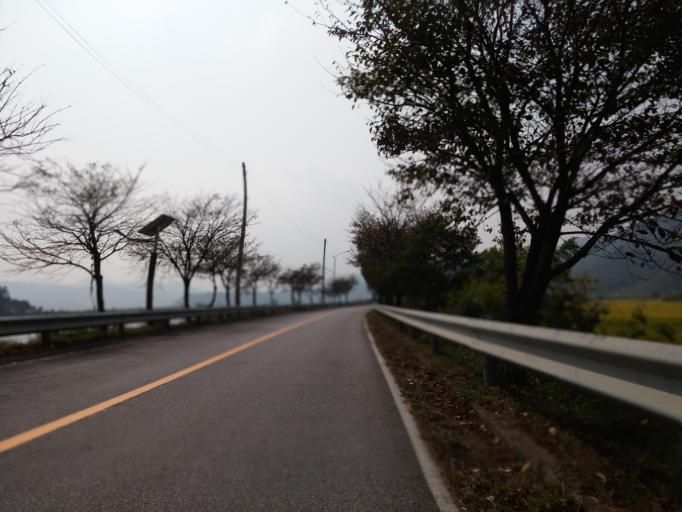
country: KR
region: Chungcheongbuk-do
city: Yong-dong
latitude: 36.3380
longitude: 127.7827
